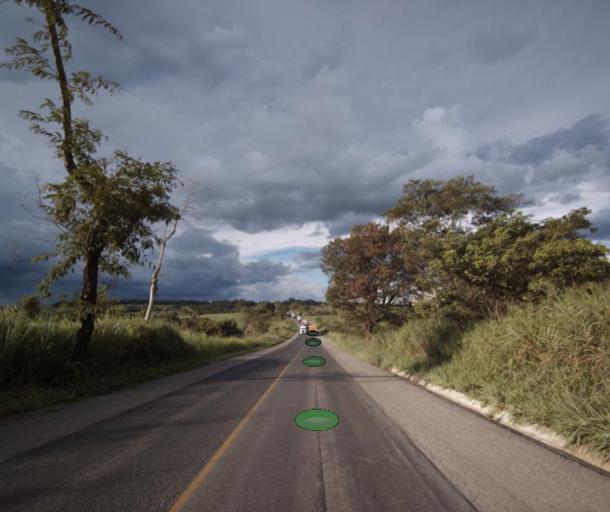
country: BR
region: Goias
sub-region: Itapaci
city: Itapaci
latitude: -15.0861
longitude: -49.4664
